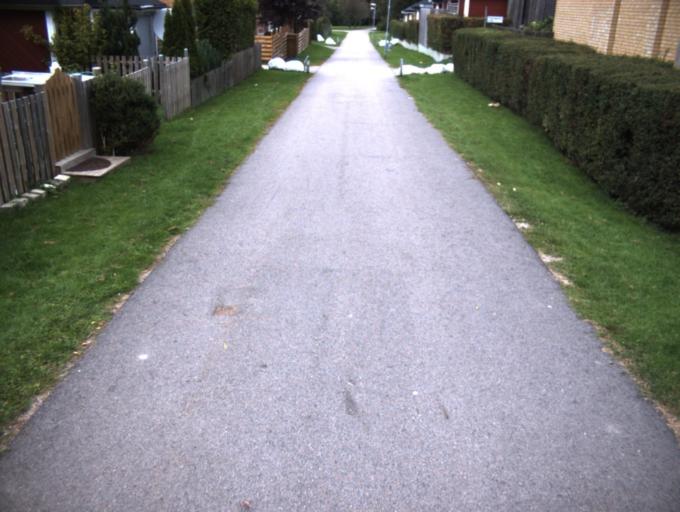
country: SE
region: Skane
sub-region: Helsingborg
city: Odakra
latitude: 56.0944
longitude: 12.7562
